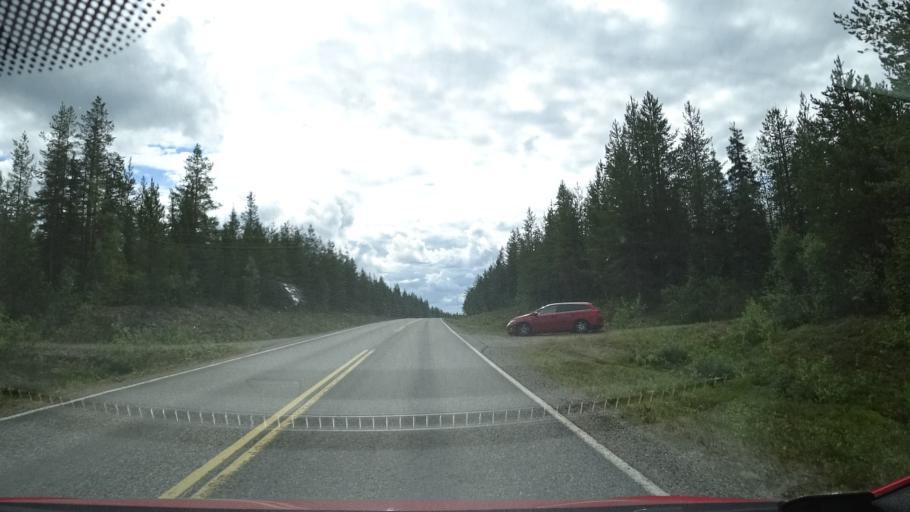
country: FI
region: Lapland
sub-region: Tunturi-Lappi
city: Kittilae
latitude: 67.5552
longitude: 24.9222
